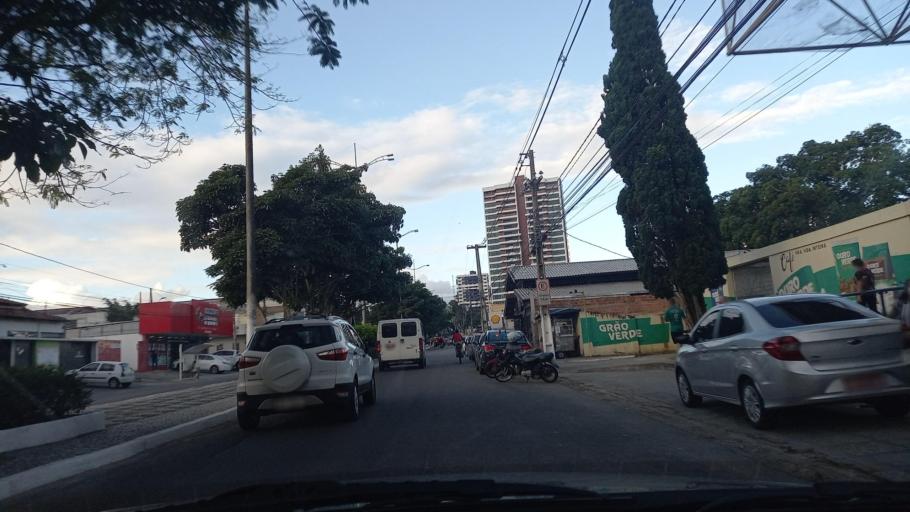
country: BR
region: Pernambuco
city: Garanhuns
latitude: -8.8830
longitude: -36.4790
